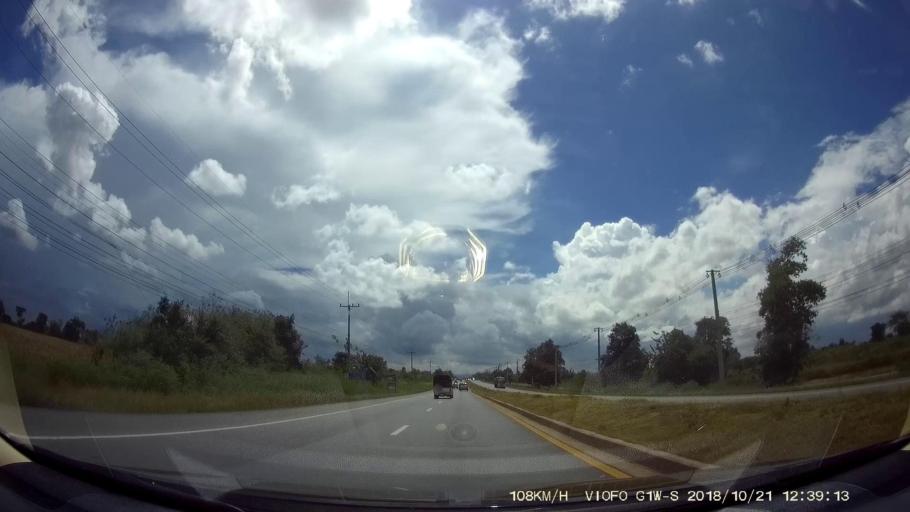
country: TH
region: Nakhon Ratchasima
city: Amphoe Sikhiu
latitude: 15.0416
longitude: 101.7017
